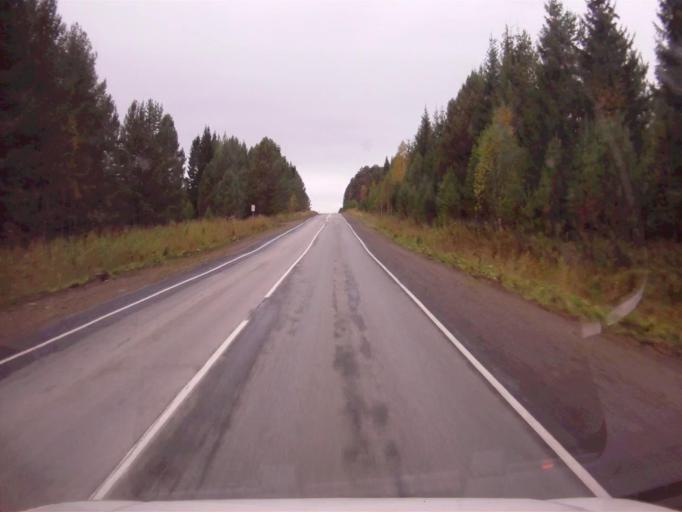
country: RU
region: Chelyabinsk
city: Nyazepetrovsk
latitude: 56.0666
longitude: 59.6770
